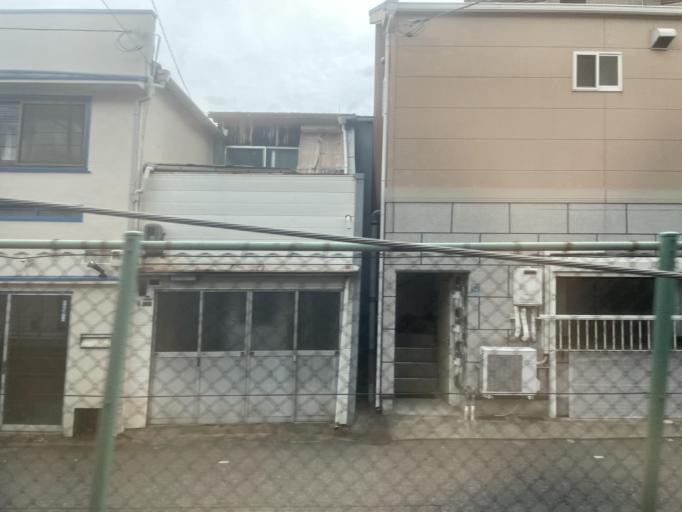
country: JP
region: Hyogo
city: Kobe
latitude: 34.7134
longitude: 135.2215
